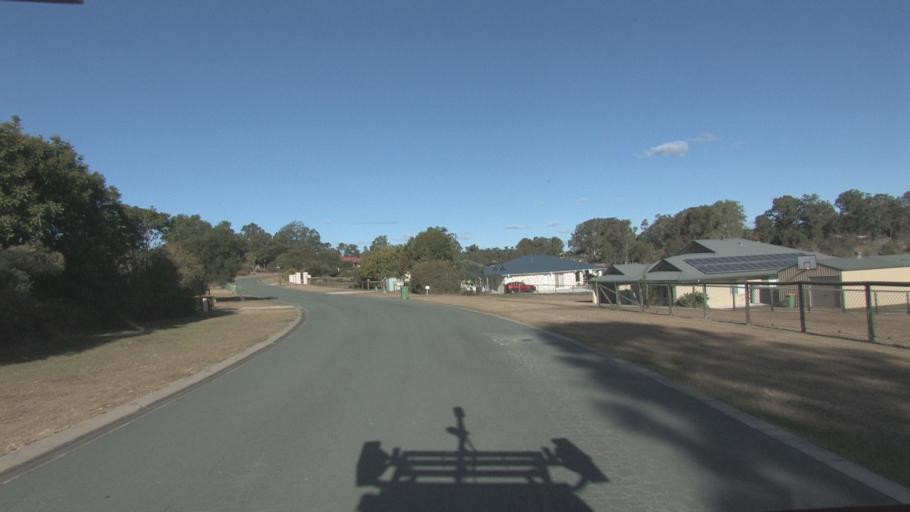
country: AU
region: Queensland
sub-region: Logan
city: North Maclean
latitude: -27.8287
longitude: 153.0025
